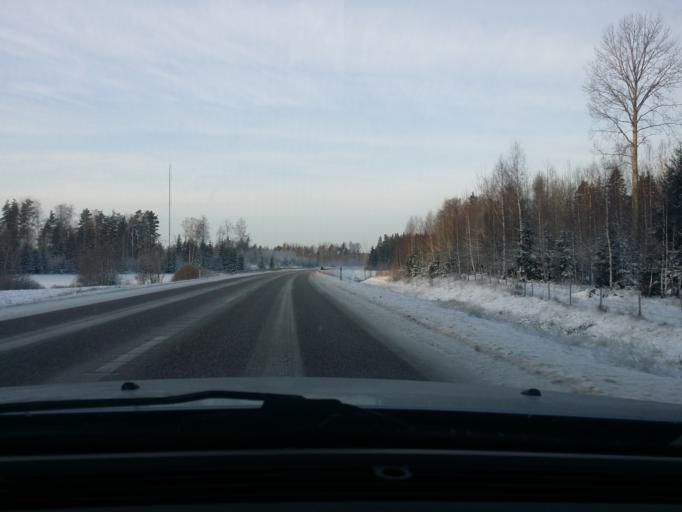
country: SE
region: OErebro
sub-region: Lindesbergs Kommun
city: Frovi
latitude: 59.4588
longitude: 15.4456
